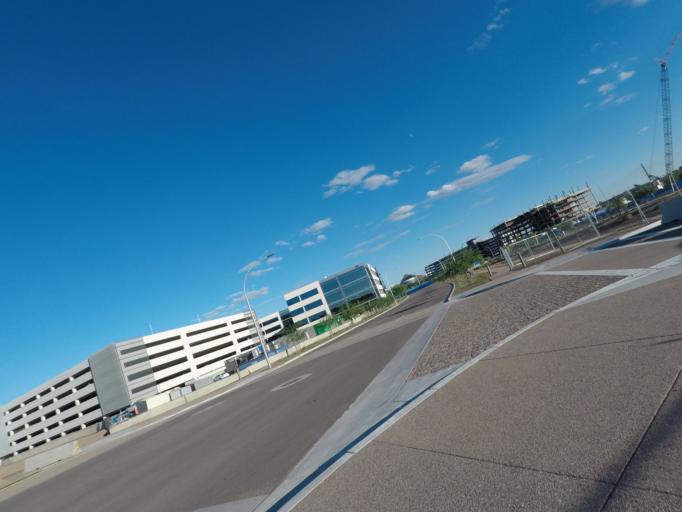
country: US
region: Arizona
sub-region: Maricopa County
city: Tempe Junction
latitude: 33.4406
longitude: -111.9576
